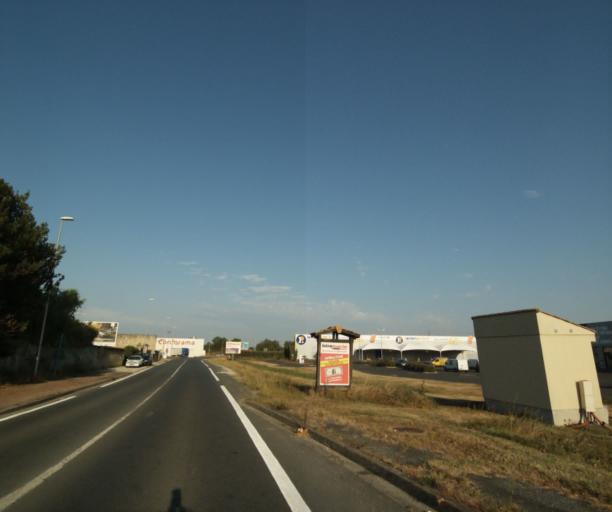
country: FR
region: Poitou-Charentes
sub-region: Departement de la Charente-Maritime
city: Tonnay-Charente
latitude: 45.9512
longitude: -0.9310
